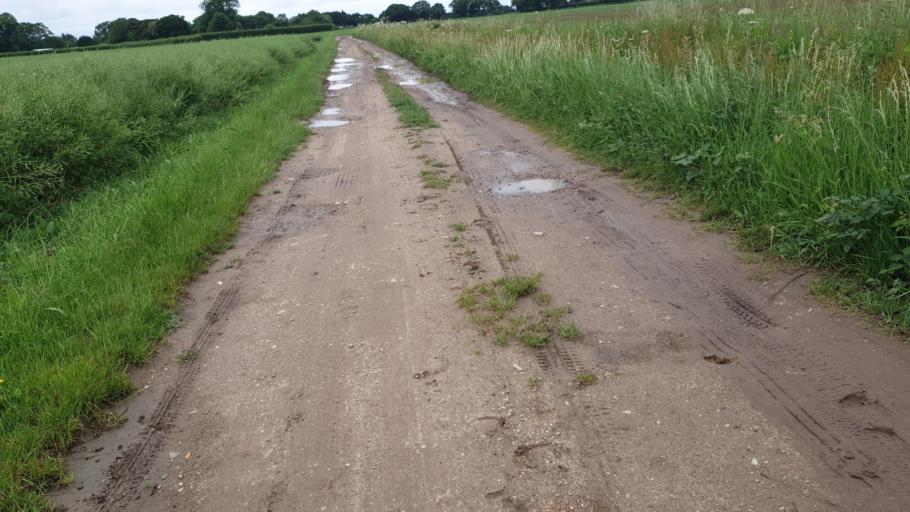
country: GB
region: England
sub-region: Essex
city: Great Bentley
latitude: 51.8823
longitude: 1.0611
